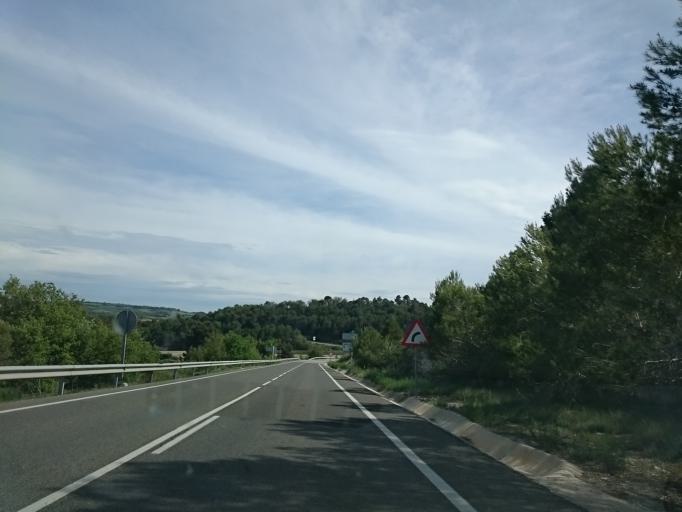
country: ES
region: Catalonia
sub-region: Provincia de Tarragona
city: Santa Coloma de Queralt
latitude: 41.5571
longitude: 1.4045
